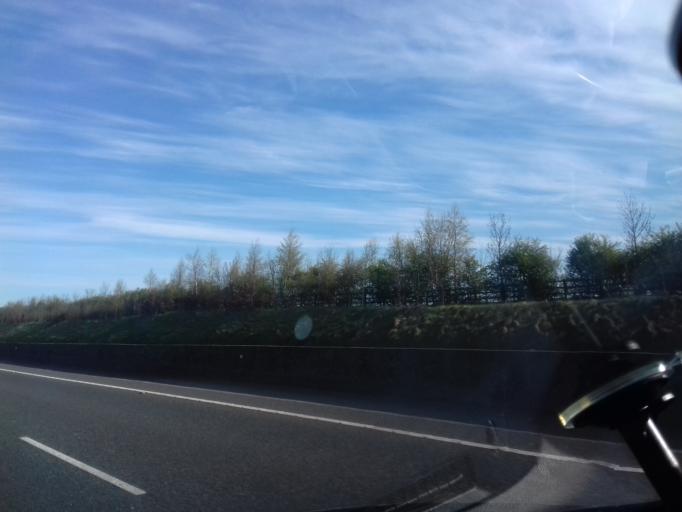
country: IE
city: Kentstown
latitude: 53.5825
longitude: -6.5793
